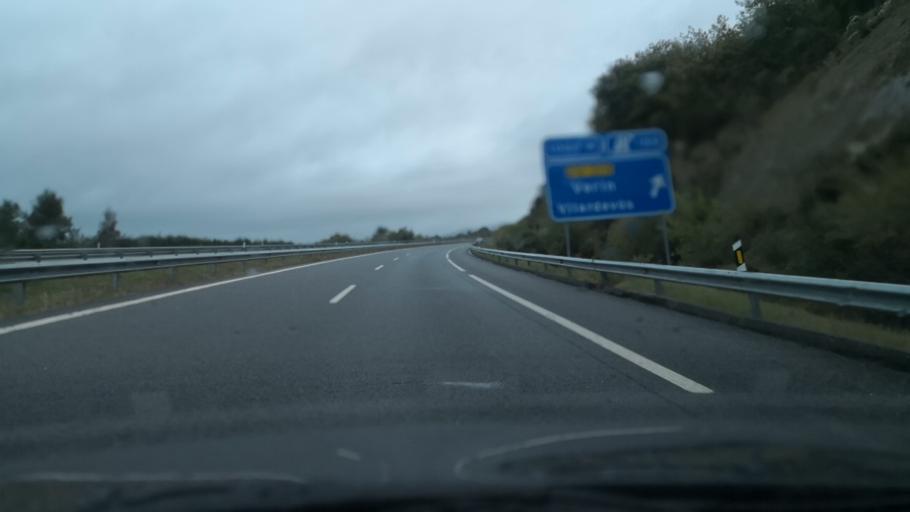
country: ES
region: Galicia
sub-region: Provincia de Ourense
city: Verin
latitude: 41.9283
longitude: -7.4085
